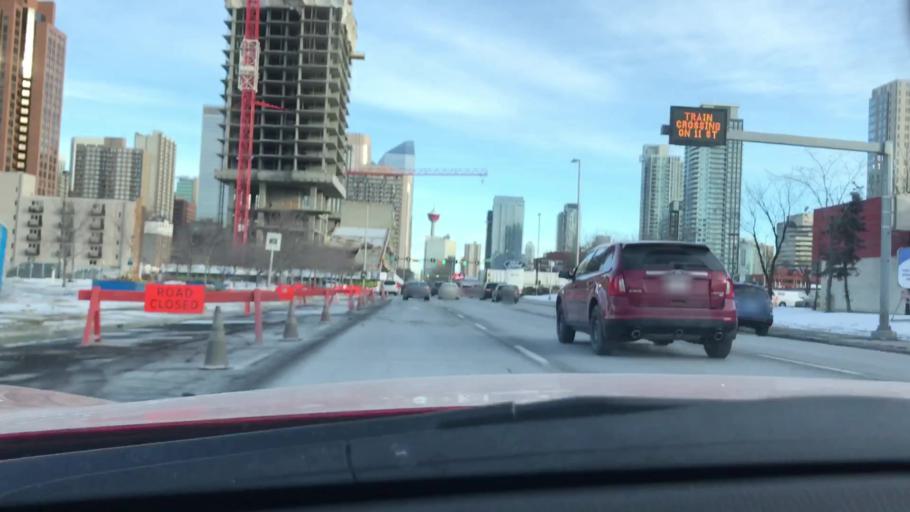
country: CA
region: Alberta
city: Calgary
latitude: 51.0455
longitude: -114.0909
